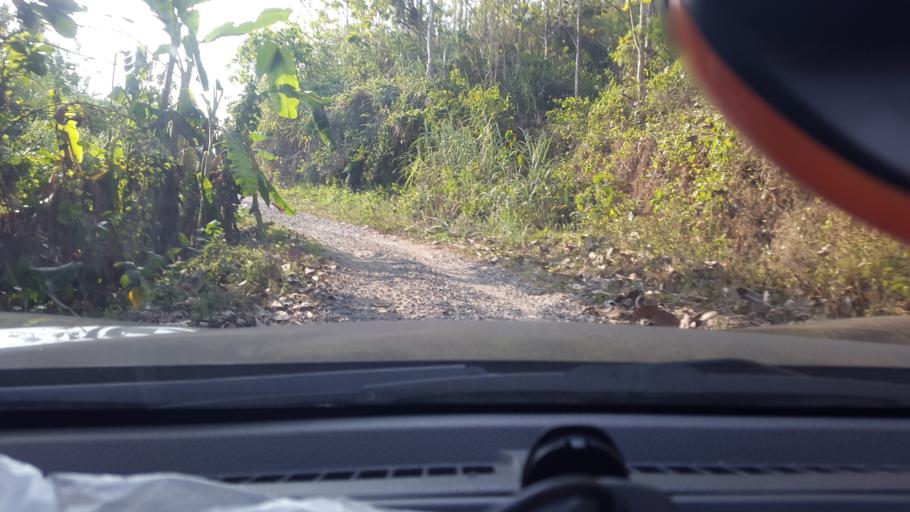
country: ID
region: West Java
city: Cikupa
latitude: -7.3561
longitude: 106.7030
